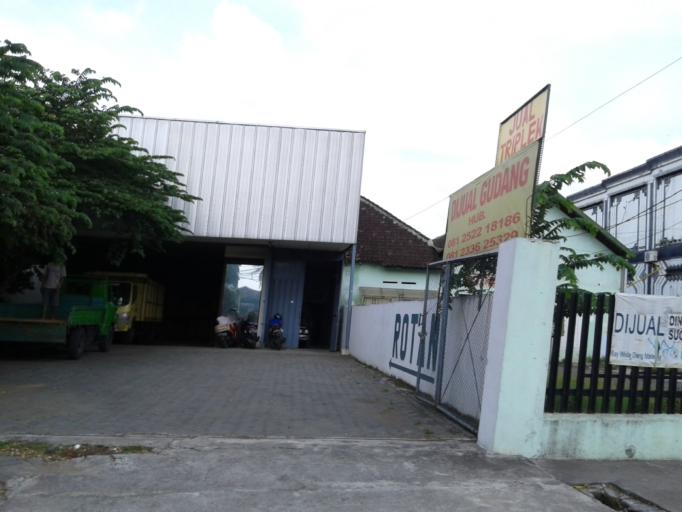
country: ID
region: East Java
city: Singosari
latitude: -7.9268
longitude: 112.6502
